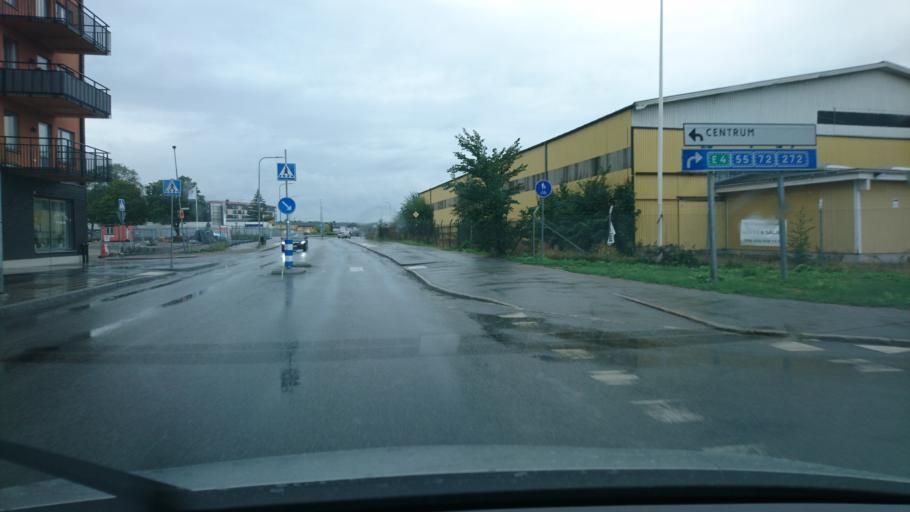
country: SE
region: Uppsala
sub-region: Uppsala Kommun
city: Uppsala
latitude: 59.8691
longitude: 17.6087
